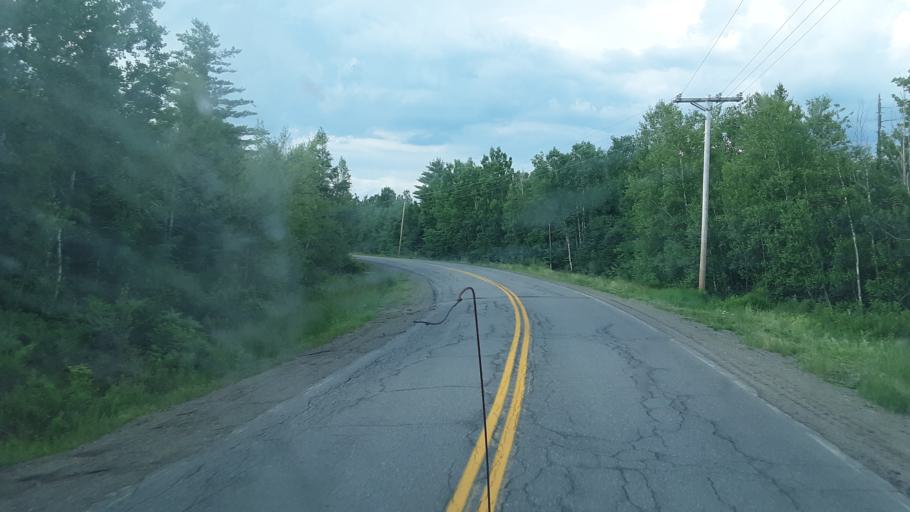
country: US
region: Maine
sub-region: Washington County
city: Calais
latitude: 45.1202
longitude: -67.4993
